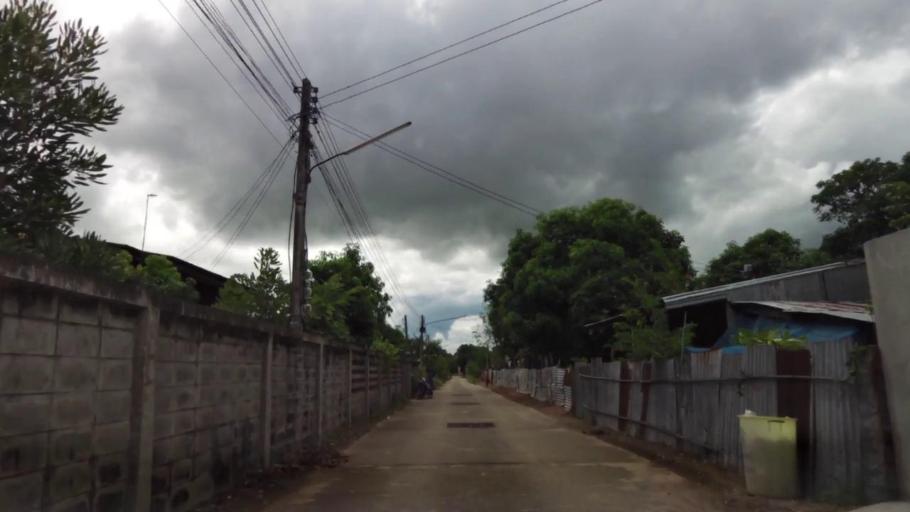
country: TH
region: Nakhon Sawan
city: Phai Sali
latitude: 15.6016
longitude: 100.6589
